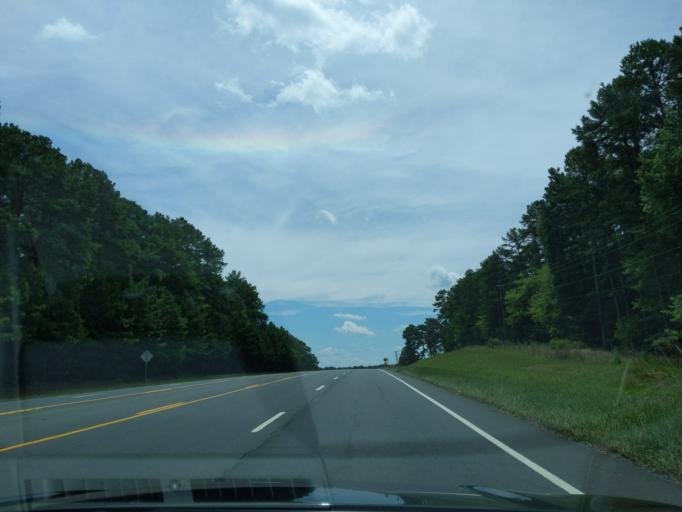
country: US
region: North Carolina
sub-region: Stanly County
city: Albemarle
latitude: 35.4561
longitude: -80.2379
